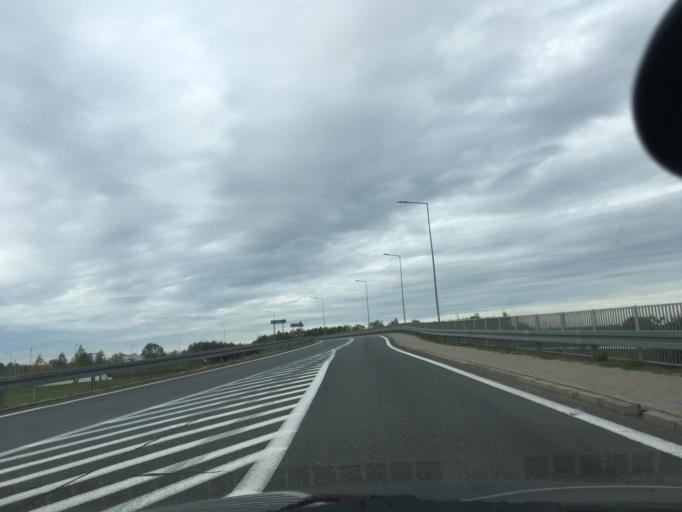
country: PL
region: Masovian Voivodeship
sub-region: Powiat zyrardowski
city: Radziejowice
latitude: 51.9715
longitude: 20.5745
